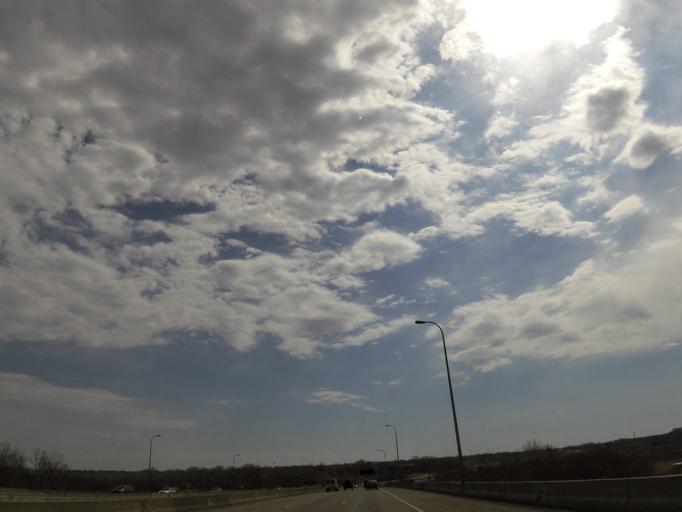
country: US
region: Minnesota
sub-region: Dakota County
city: Eagan
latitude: 44.8265
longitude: -93.2305
